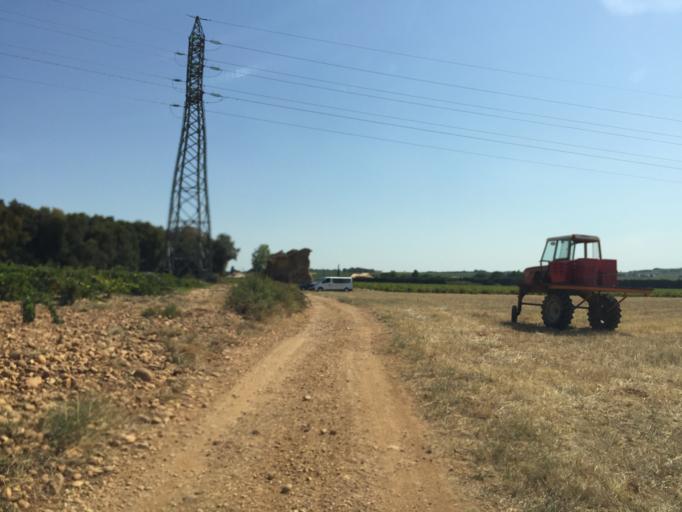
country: FR
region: Provence-Alpes-Cote d'Azur
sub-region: Departement du Vaucluse
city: Orange
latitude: 44.1077
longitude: 4.8346
